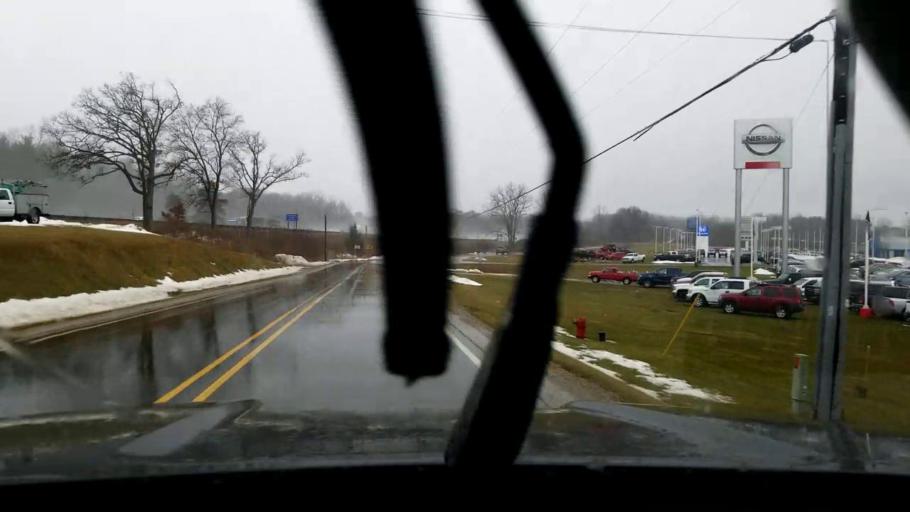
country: US
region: Michigan
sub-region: Jackson County
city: Jackson
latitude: 42.2771
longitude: -84.3750
